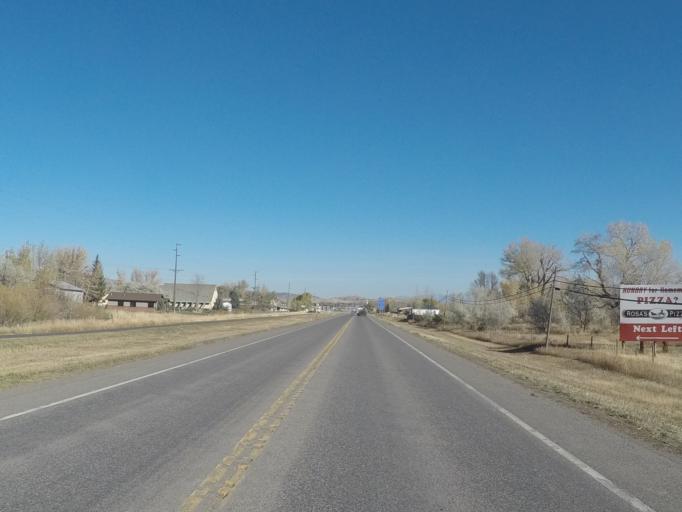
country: US
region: Montana
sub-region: Park County
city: Livingston
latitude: 45.6306
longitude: -110.5766
